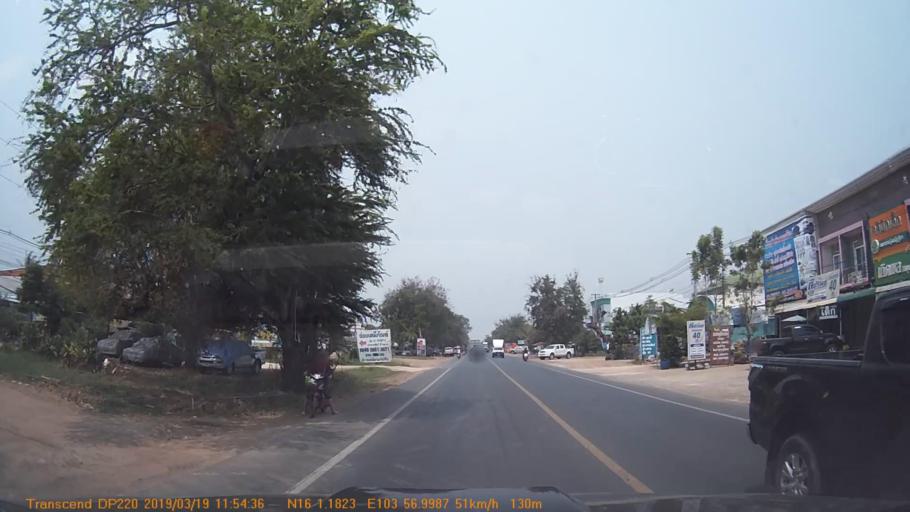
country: TH
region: Roi Et
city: Ban Selaphum
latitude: 16.0198
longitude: 103.9499
